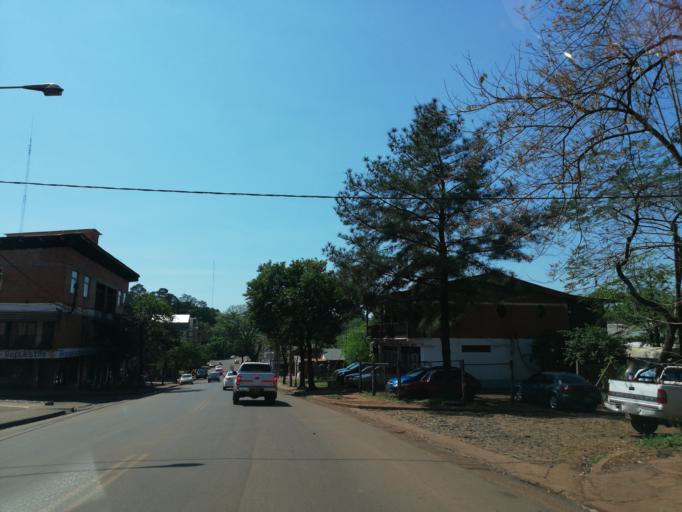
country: AR
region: Misiones
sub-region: Departamento de Eldorado
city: Eldorado
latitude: -26.4057
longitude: -54.6161
